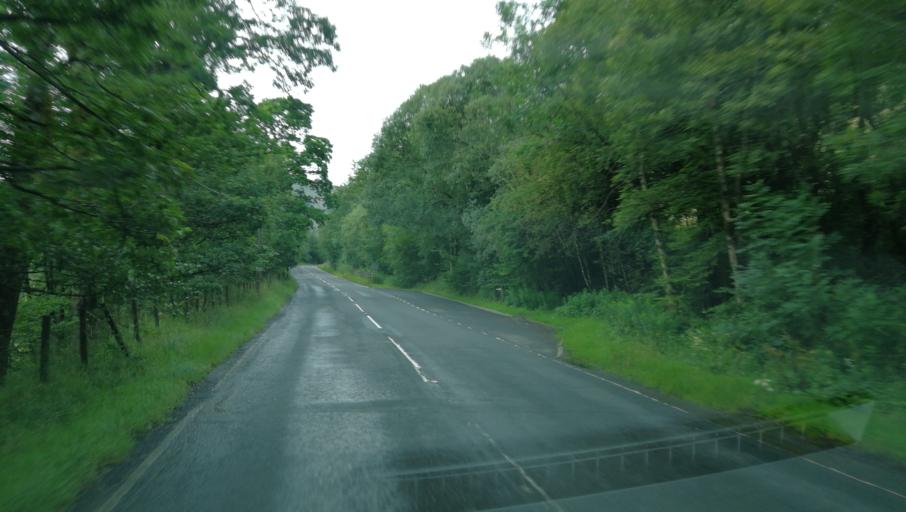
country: GB
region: Scotland
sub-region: Stirling
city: Callander
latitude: 56.3363
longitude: -4.3245
